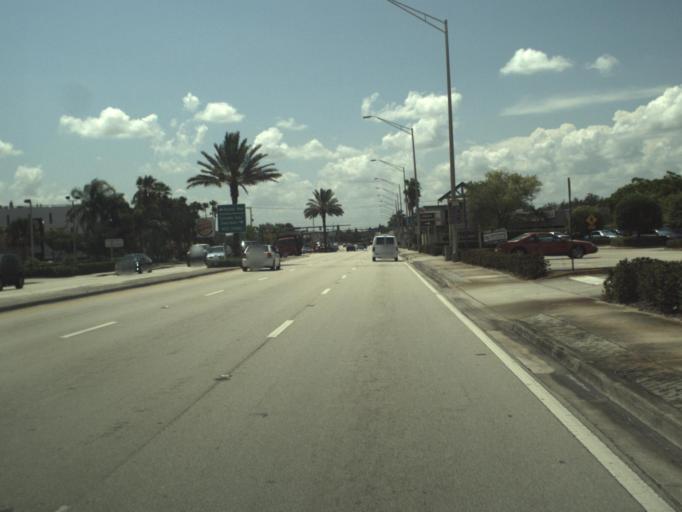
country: US
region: Florida
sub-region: Martin County
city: Stuart
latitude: 27.1900
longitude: -80.2504
